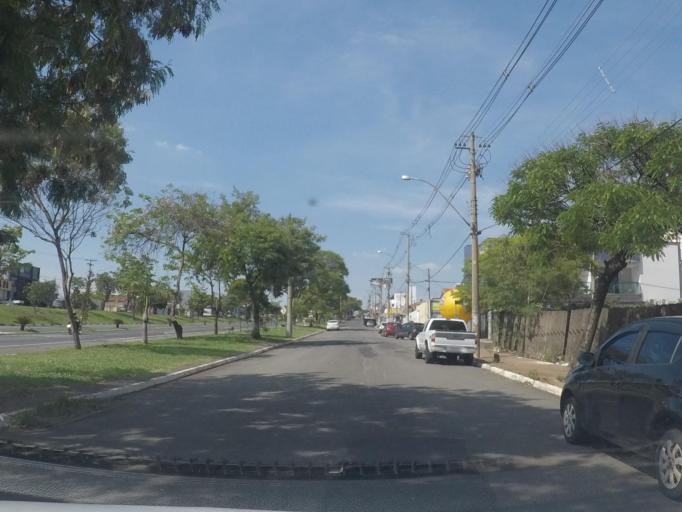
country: BR
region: Sao Paulo
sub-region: Sumare
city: Sumare
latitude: -22.8168
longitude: -47.2606
